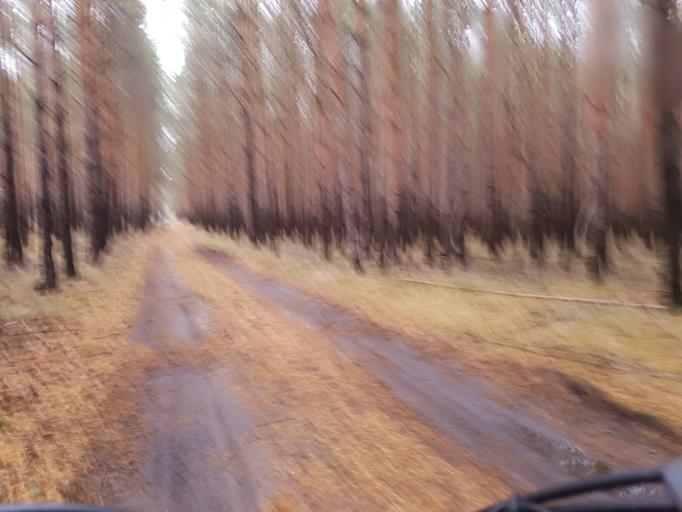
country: DE
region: Brandenburg
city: Schilda
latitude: 51.6221
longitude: 13.3704
